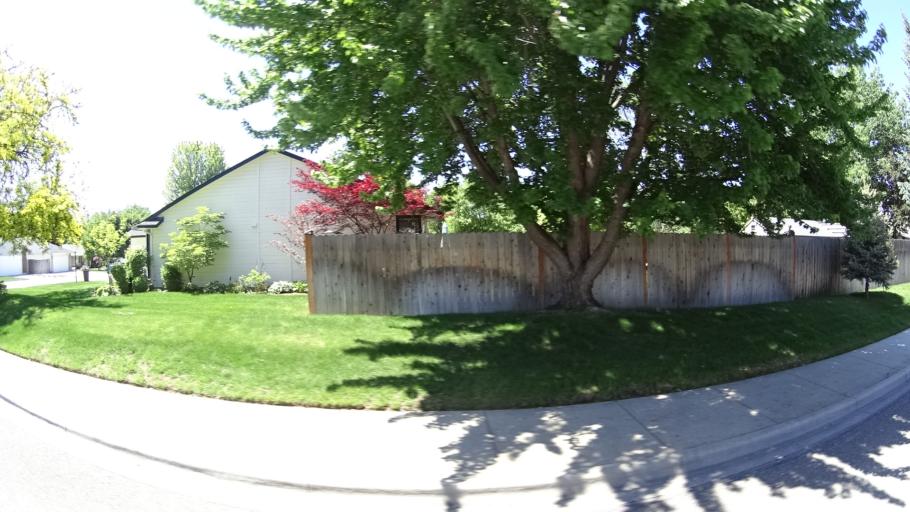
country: US
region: Idaho
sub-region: Ada County
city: Boise
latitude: 43.5662
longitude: -116.1468
